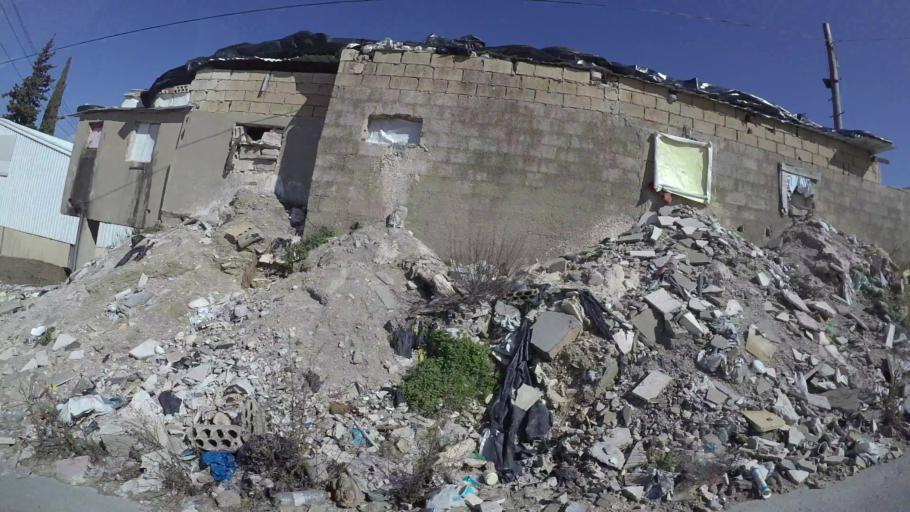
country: JO
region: Amman
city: Al Bunayyat ash Shamaliyah
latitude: 31.9132
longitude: 35.9054
